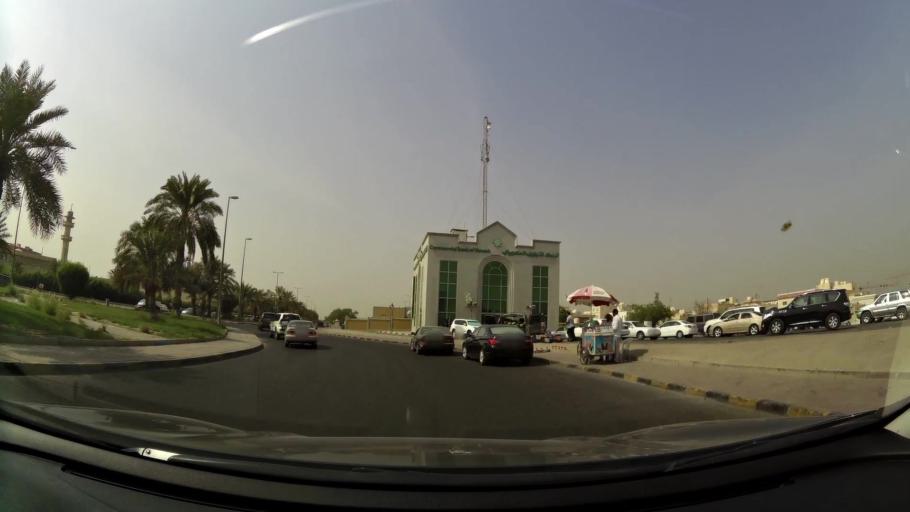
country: KW
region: Al Asimah
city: Ar Rabiyah
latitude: 29.3034
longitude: 47.8790
